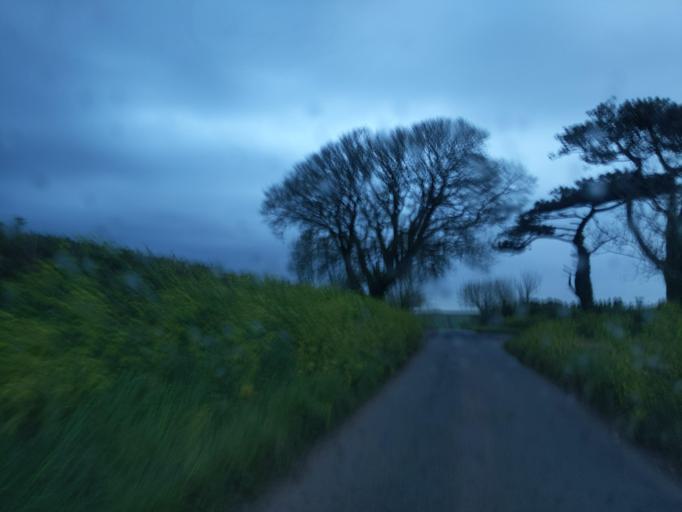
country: GB
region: England
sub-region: Devon
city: Dartmouth
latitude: 50.3604
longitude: -3.5478
